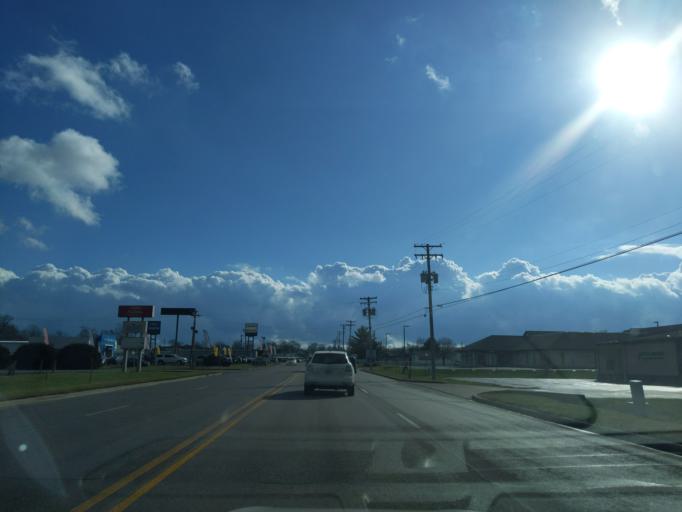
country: US
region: Indiana
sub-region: Decatur County
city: Greensburg
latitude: 39.3470
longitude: -85.4963
